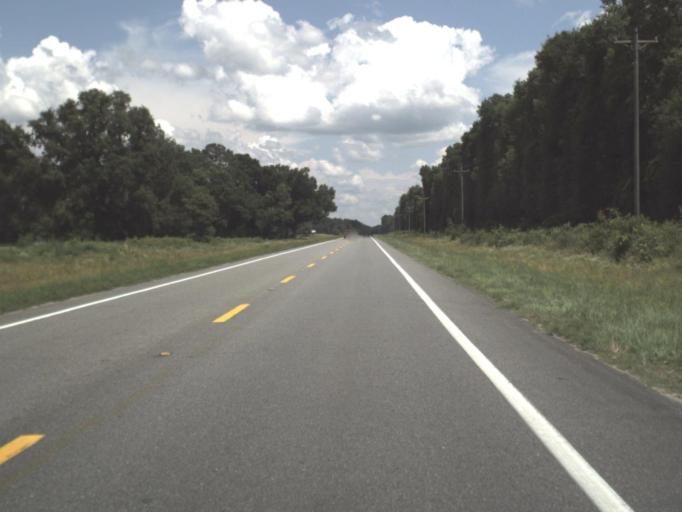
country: US
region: Florida
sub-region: Alachua County
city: High Springs
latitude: 29.9029
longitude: -82.6899
